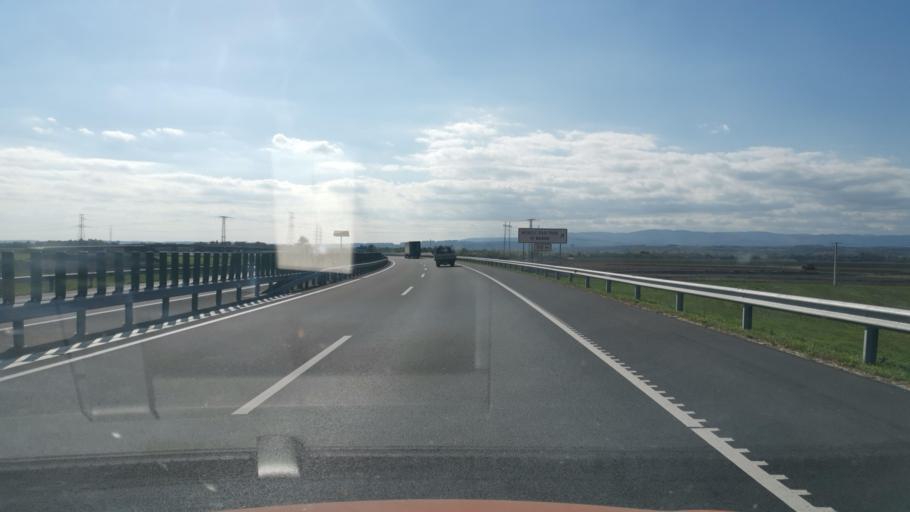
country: HU
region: Borsod-Abauj-Zemplen
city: Arnot
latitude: 48.1421
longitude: 20.8378
